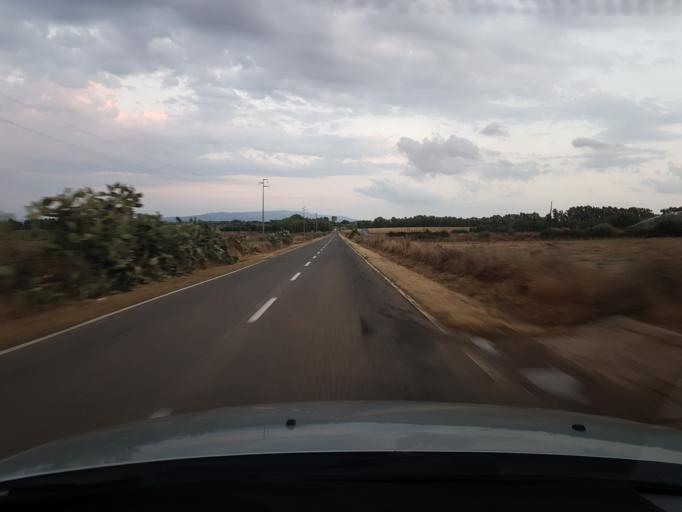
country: IT
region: Sardinia
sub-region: Provincia di Oristano
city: Tramatza
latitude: 40.0164
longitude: 8.6439
